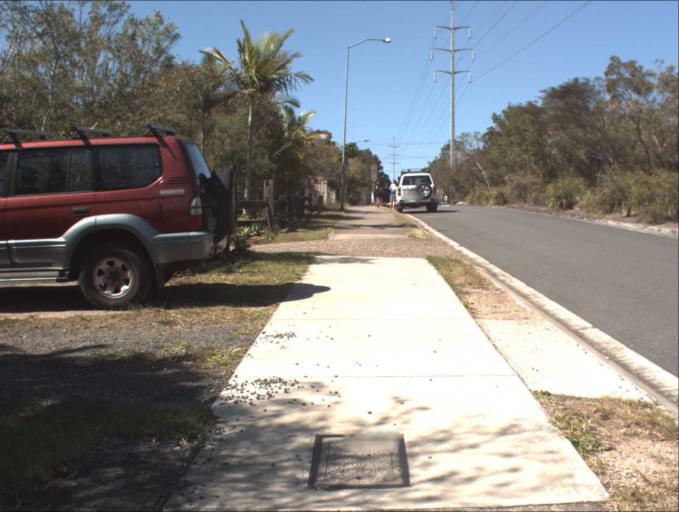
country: AU
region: Queensland
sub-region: Logan
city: Springwood
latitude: -27.6144
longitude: 153.1426
